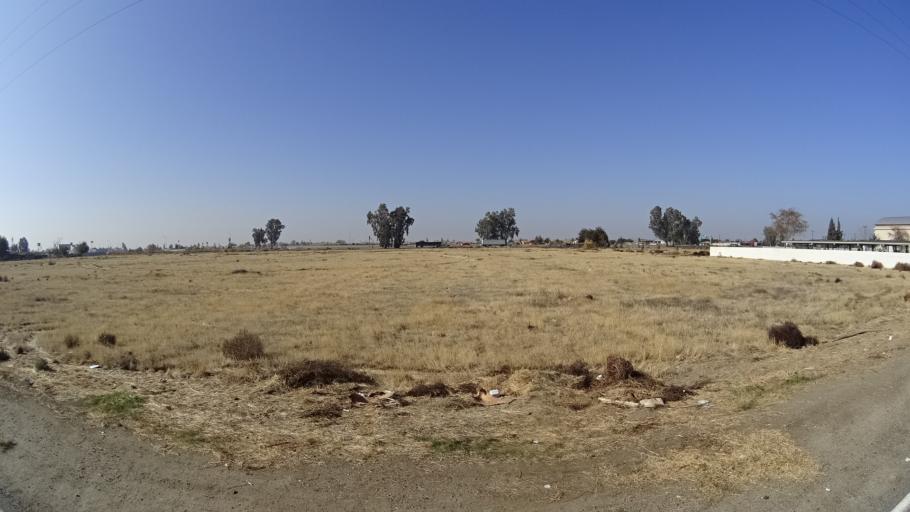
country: US
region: California
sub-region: Kern County
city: Greenfield
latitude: 35.2716
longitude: -119.0210
